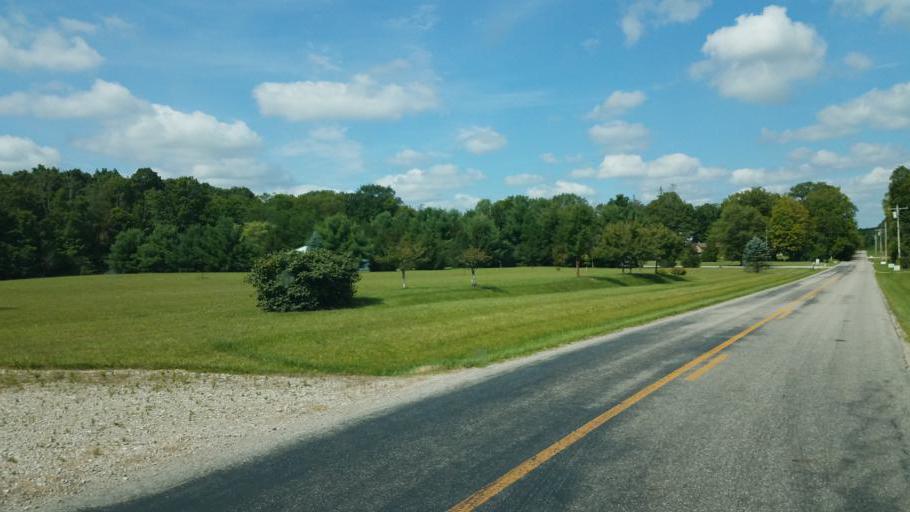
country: US
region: Ohio
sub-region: Delaware County
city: Sunbury
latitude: 40.2893
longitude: -82.9455
